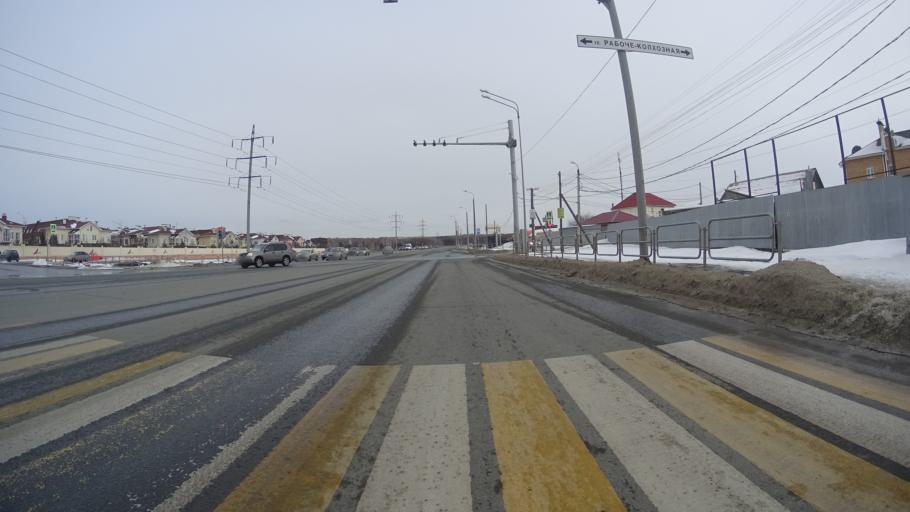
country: RU
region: Chelyabinsk
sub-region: Gorod Chelyabinsk
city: Chelyabinsk
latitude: 55.1552
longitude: 61.3136
